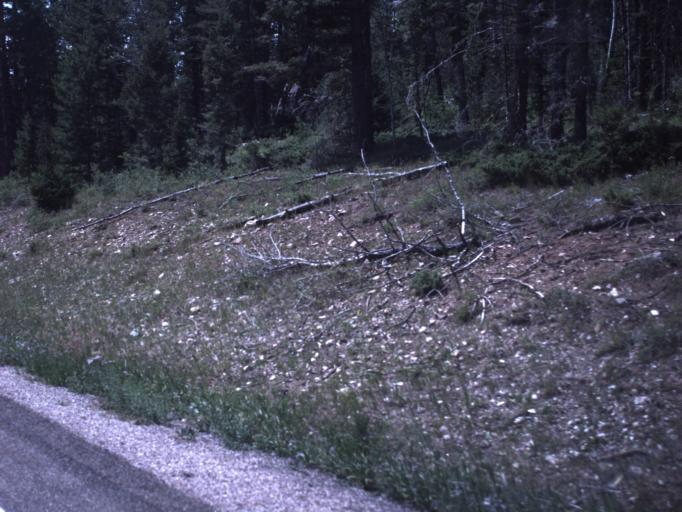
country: US
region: Utah
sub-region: Uintah County
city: Maeser
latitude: 40.7356
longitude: -109.4708
